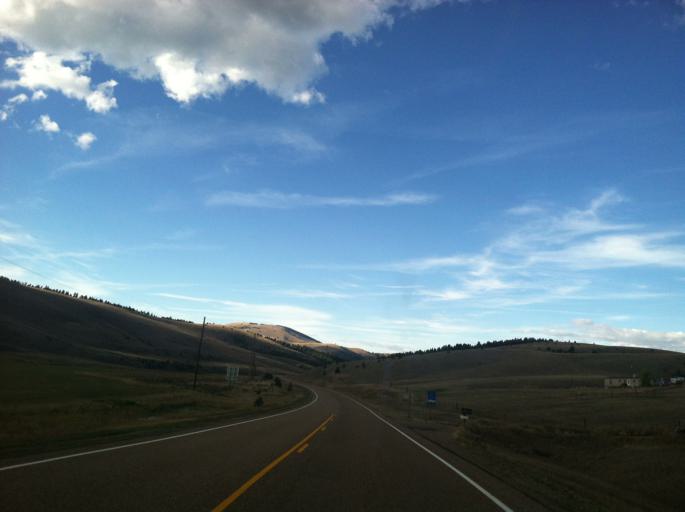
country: US
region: Montana
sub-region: Granite County
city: Philipsburg
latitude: 46.3755
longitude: -113.3130
